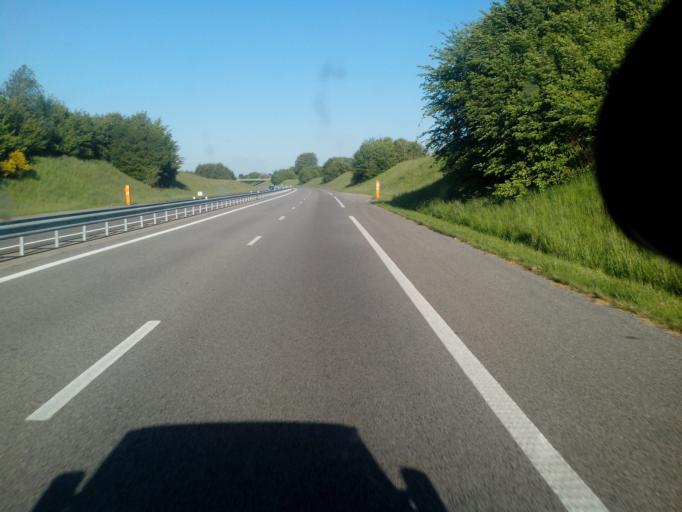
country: FR
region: Haute-Normandie
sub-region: Departement de la Seine-Maritime
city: Nointot
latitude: 49.6036
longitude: 0.4835
